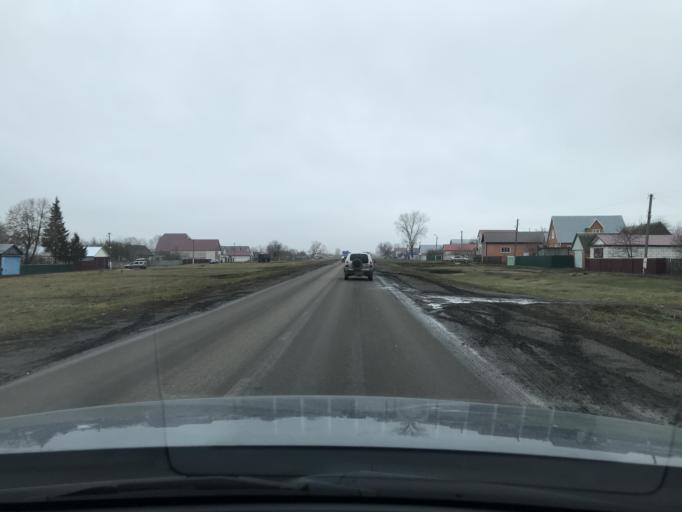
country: RU
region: Penza
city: Zemetchino
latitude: 53.5083
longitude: 42.6377
